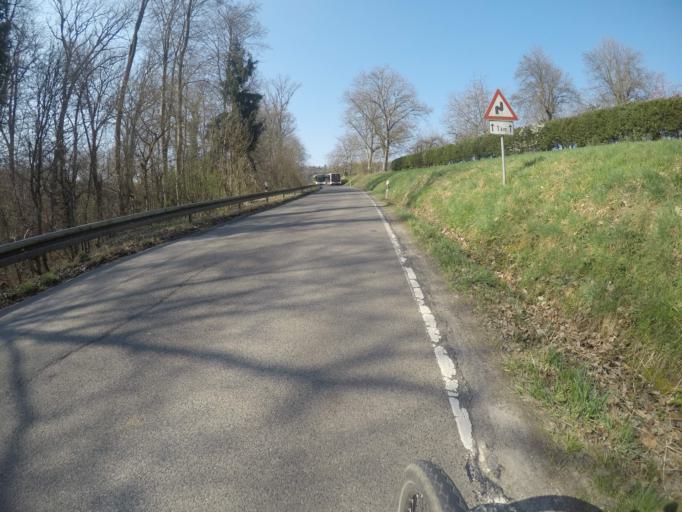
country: DE
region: Baden-Wuerttemberg
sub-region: Regierungsbezirk Stuttgart
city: Altenriet
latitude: 48.5805
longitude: 9.2261
